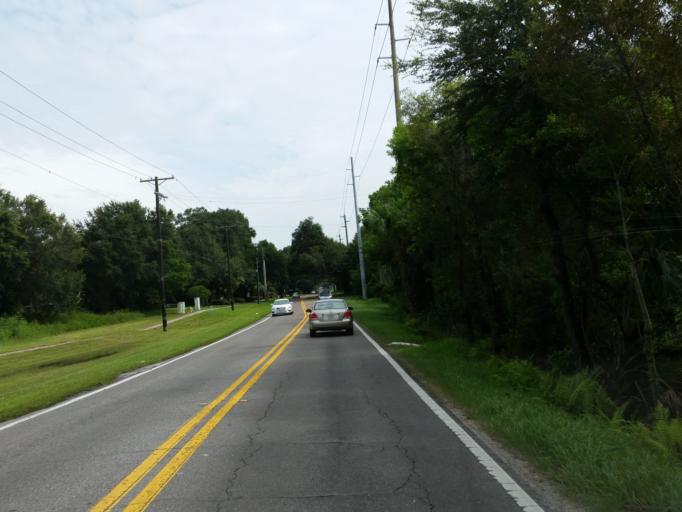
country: US
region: Florida
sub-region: Hillsborough County
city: Valrico
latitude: 27.9402
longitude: -82.2528
